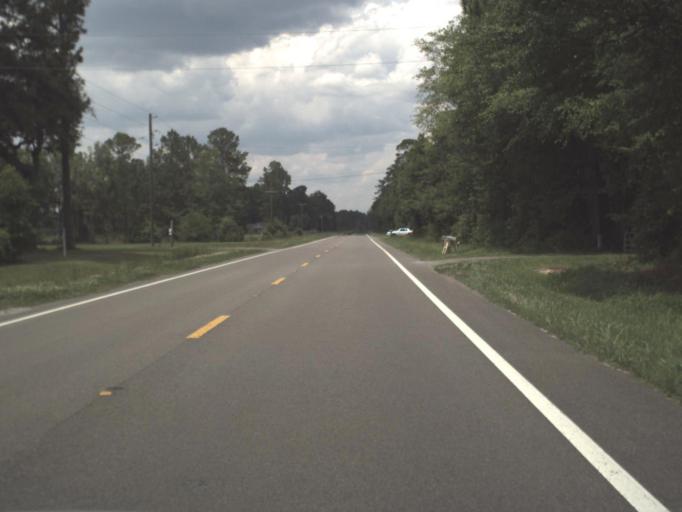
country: US
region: Florida
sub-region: Columbia County
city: Five Points
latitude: 30.3003
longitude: -82.6308
